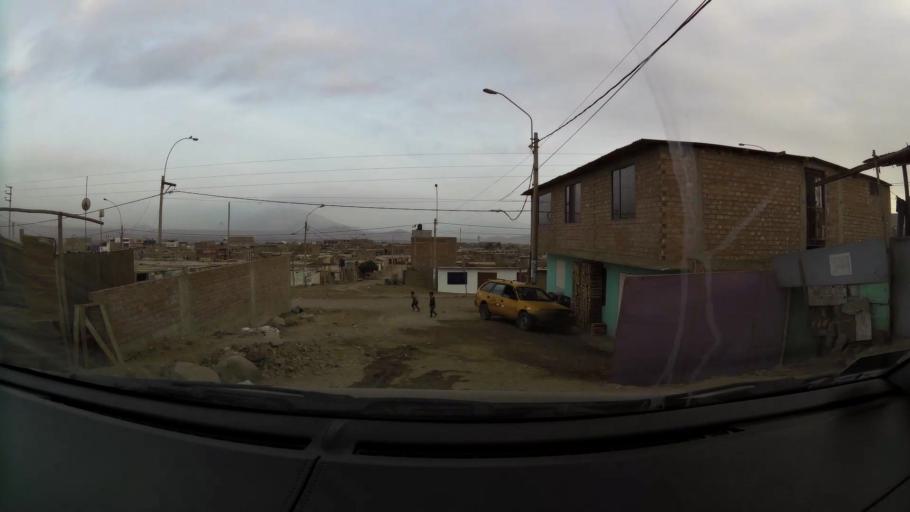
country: PE
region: Lima
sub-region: Lima
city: Santa Rosa
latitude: -11.7306
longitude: -77.1436
